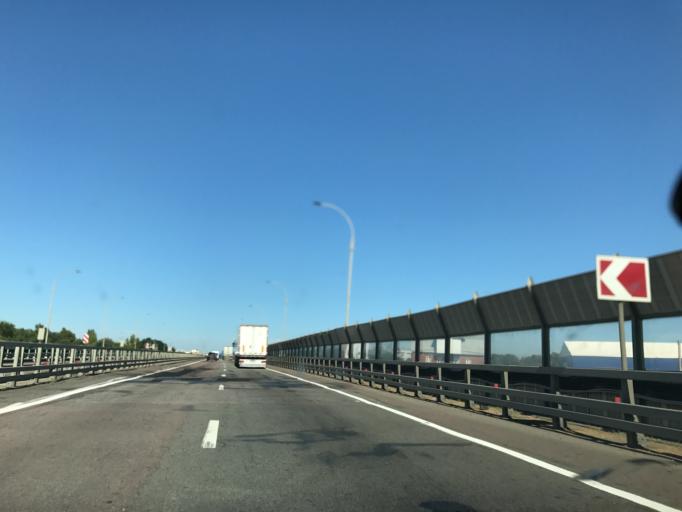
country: RU
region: Voronezj
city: Verkhniy Mamon
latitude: 50.1766
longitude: 40.4263
